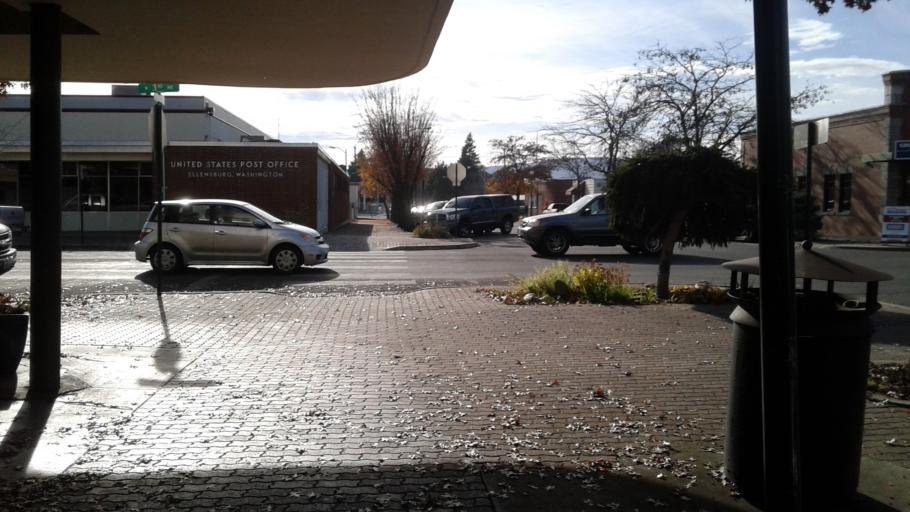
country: US
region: Washington
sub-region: Kittitas County
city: Ellensburg
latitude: 46.9946
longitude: -120.5472
